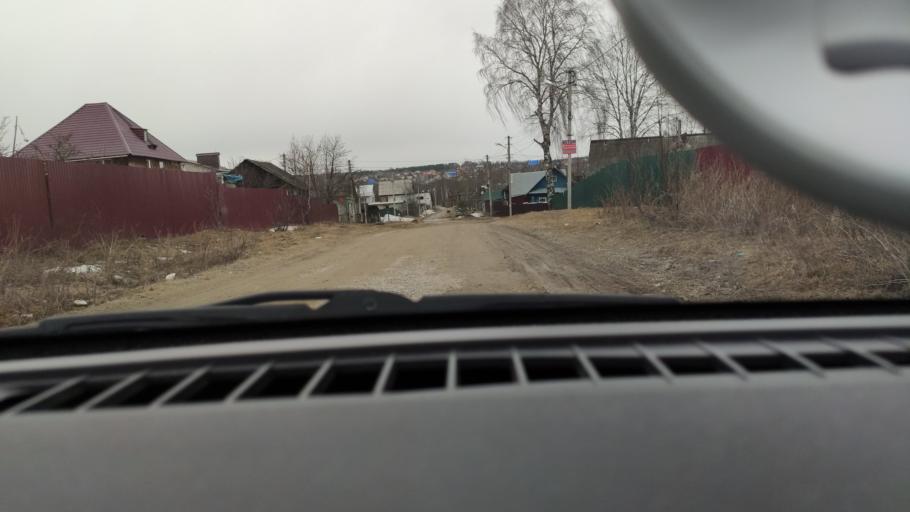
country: RU
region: Perm
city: Kondratovo
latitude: 58.0505
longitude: 56.0415
